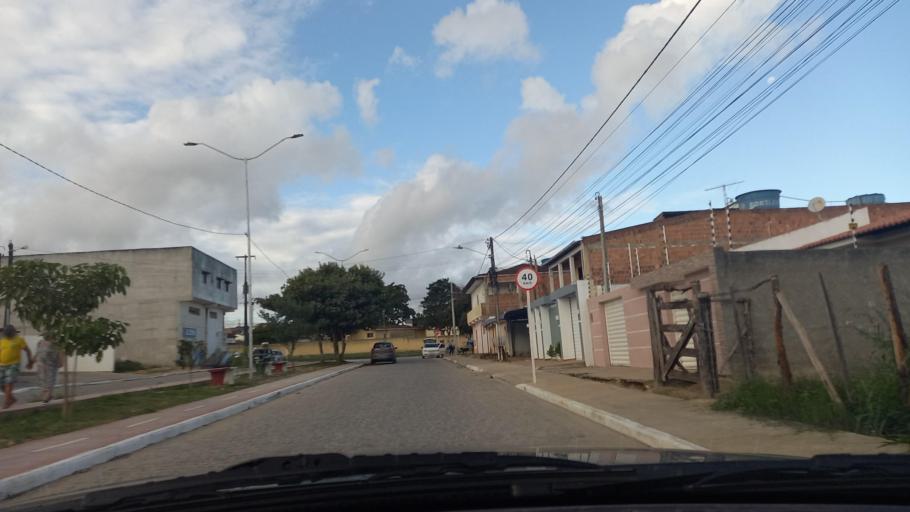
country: BR
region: Pernambuco
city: Garanhuns
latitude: -8.9091
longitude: -36.4834
